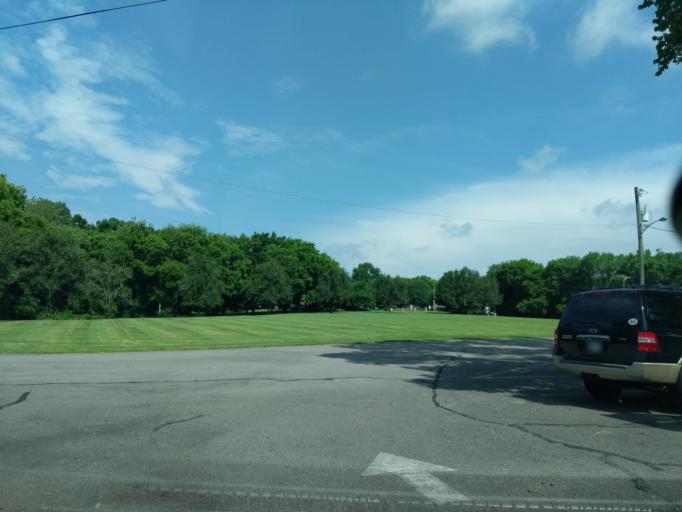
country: US
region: Tennessee
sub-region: Davidson County
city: Goodlettsville
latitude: 36.3051
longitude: -86.7096
